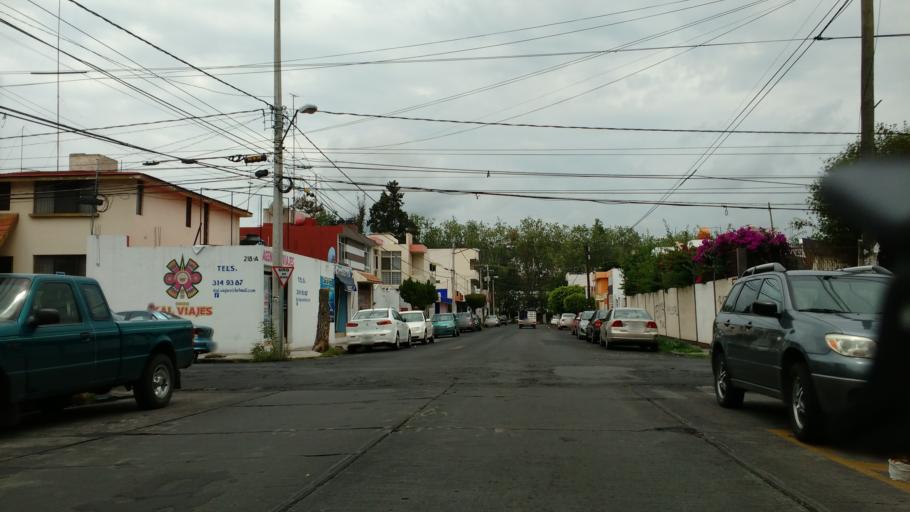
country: MX
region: Michoacan
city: Morelia
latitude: 19.6921
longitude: -101.1770
